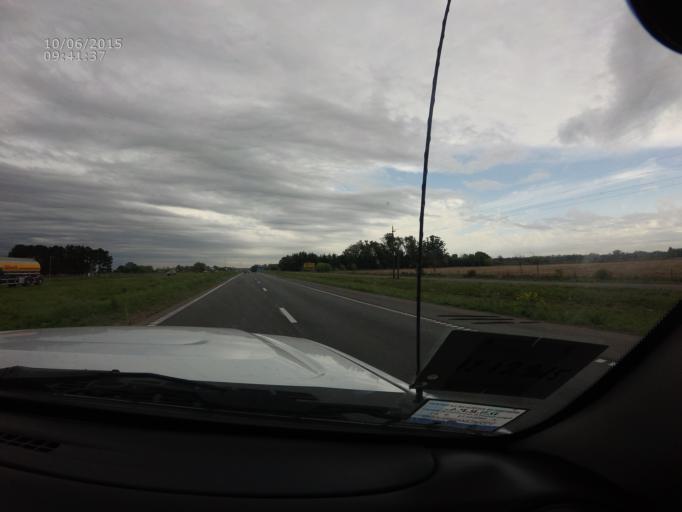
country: AR
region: Buenos Aires
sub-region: Partido de Zarate
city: Zarate
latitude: -34.0765
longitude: -59.2207
